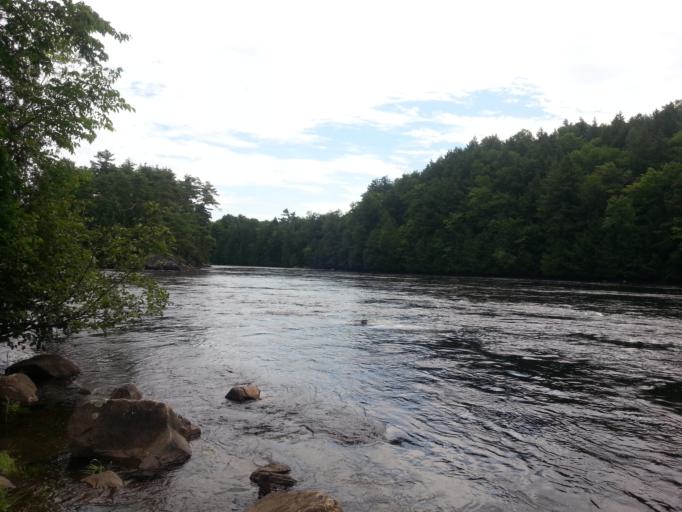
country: CA
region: Ontario
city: Renfrew
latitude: 45.3210
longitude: -76.6842
